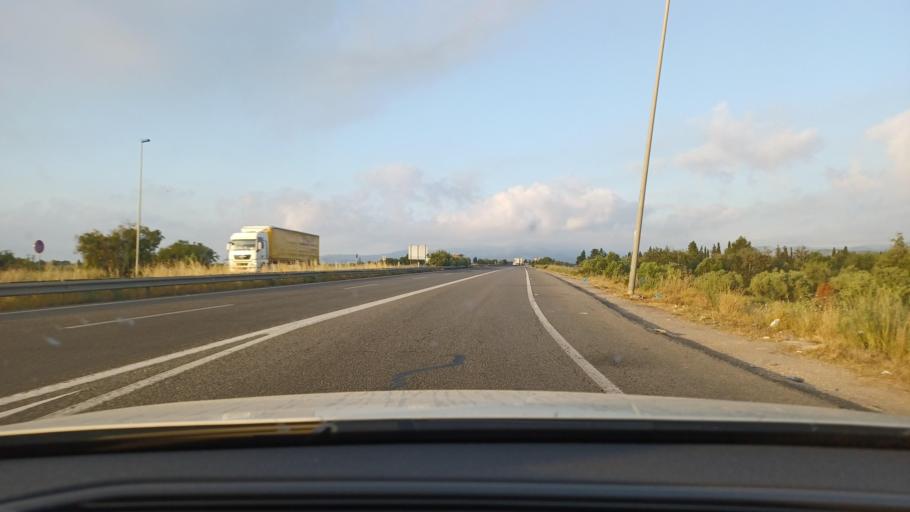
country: ES
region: Valencia
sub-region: Provincia de Castello
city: Benicarlo
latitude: 40.4577
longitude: 0.4053
